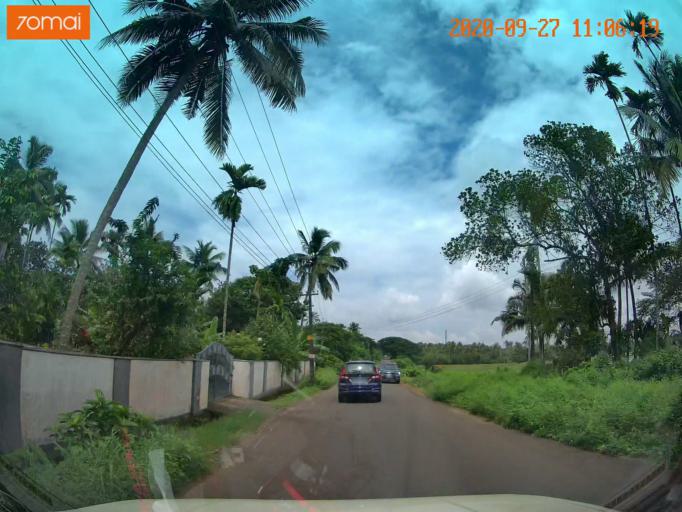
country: IN
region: Kerala
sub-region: Thrissur District
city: Irinjalakuda
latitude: 10.4250
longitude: 76.2428
